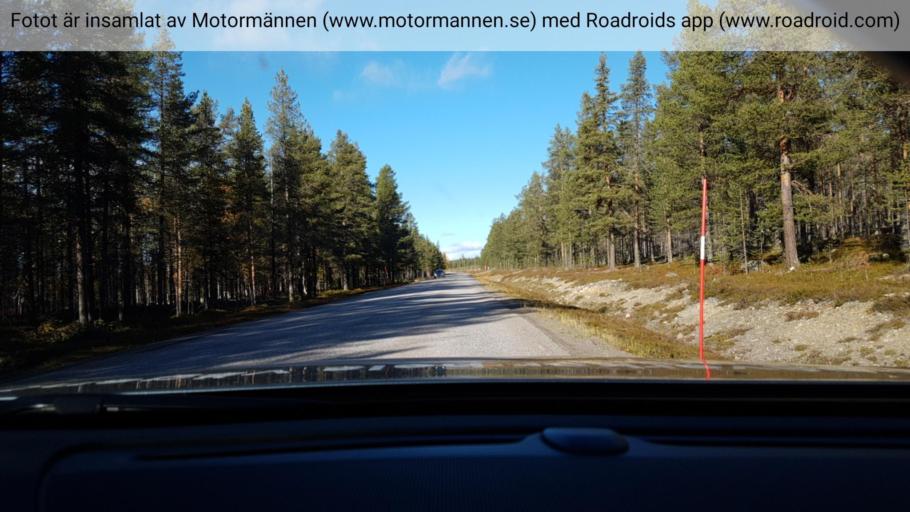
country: SE
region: Vaesterbotten
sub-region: Mala Kommun
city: Mala
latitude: 65.7682
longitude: 18.5417
